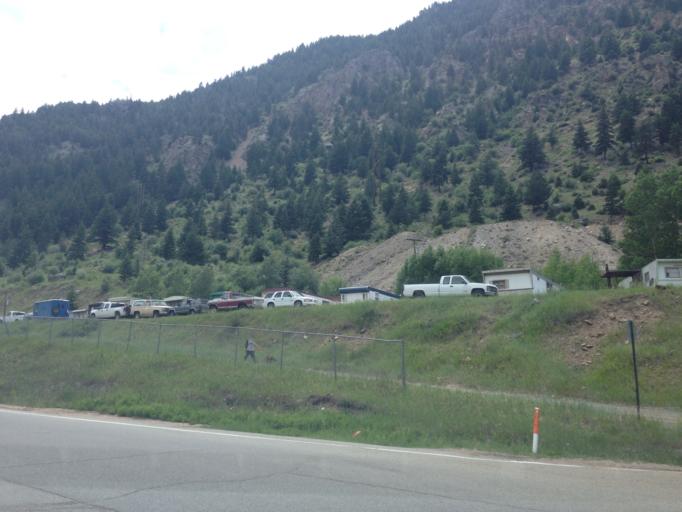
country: US
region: Colorado
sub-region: Clear Creek County
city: Georgetown
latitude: 39.7154
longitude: -105.6969
